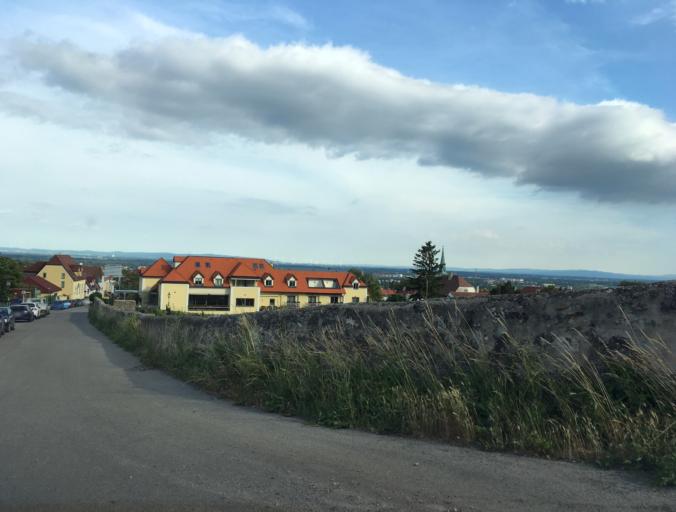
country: AT
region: Lower Austria
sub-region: Politischer Bezirk Modling
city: Gumpoldskirchen
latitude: 48.0478
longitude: 16.2758
